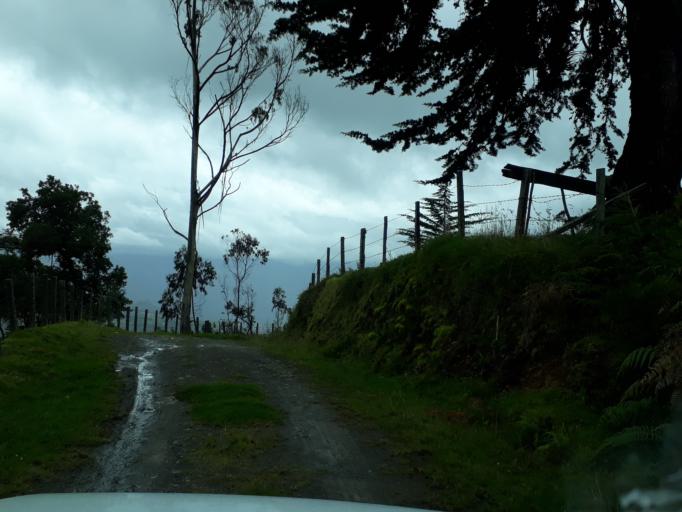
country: CO
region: Cundinamarca
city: Junin
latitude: 4.7329
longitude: -73.6258
